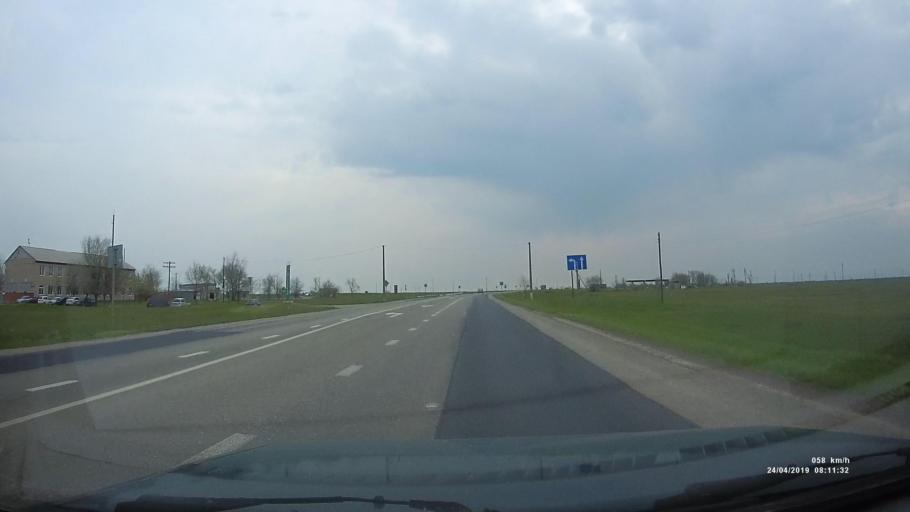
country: RU
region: Kalmykiya
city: Priyutnoye
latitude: 46.1024
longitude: 43.5294
